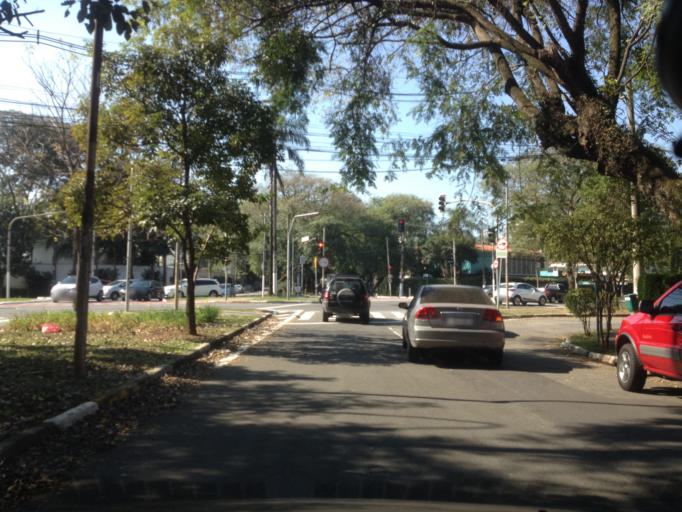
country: BR
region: Sao Paulo
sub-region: Sao Paulo
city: Sao Paulo
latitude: -23.5558
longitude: -46.7056
